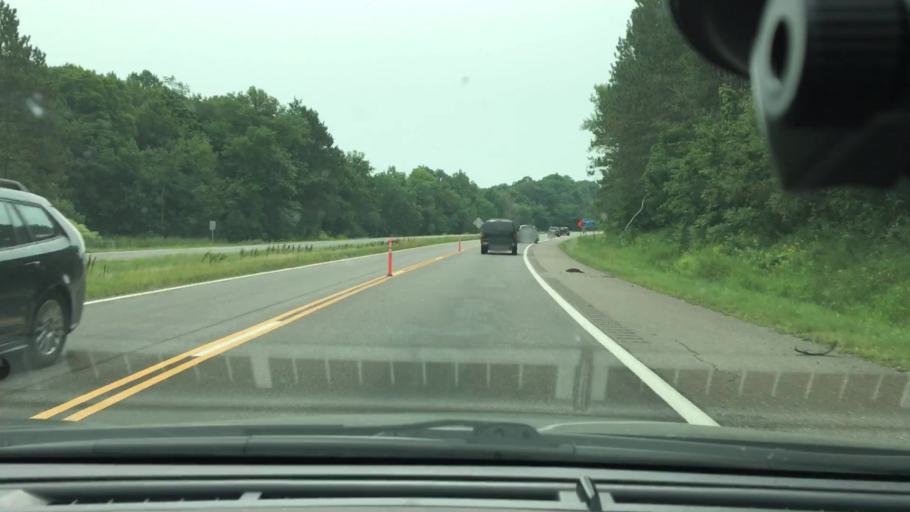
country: US
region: Minnesota
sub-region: Mille Lacs County
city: Vineland
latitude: 46.2845
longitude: -93.8210
